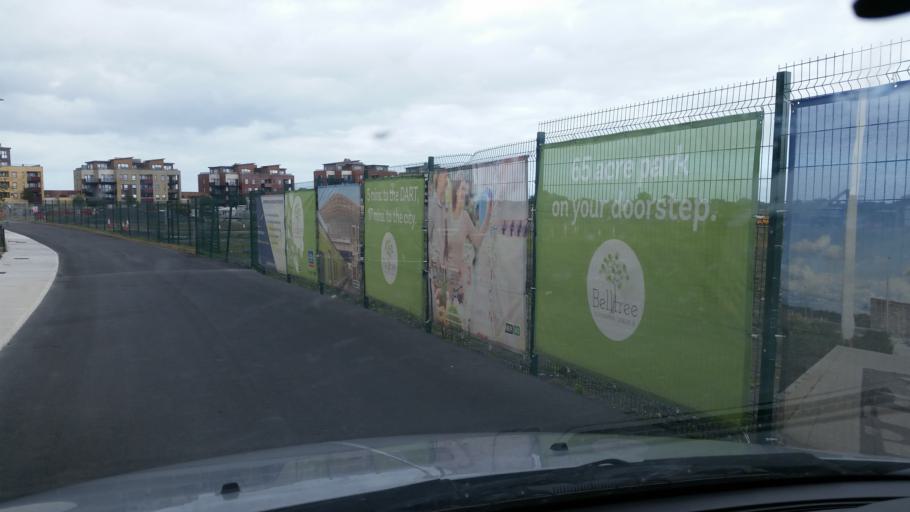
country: IE
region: Leinster
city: Donaghmede
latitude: 53.4056
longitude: -6.1567
